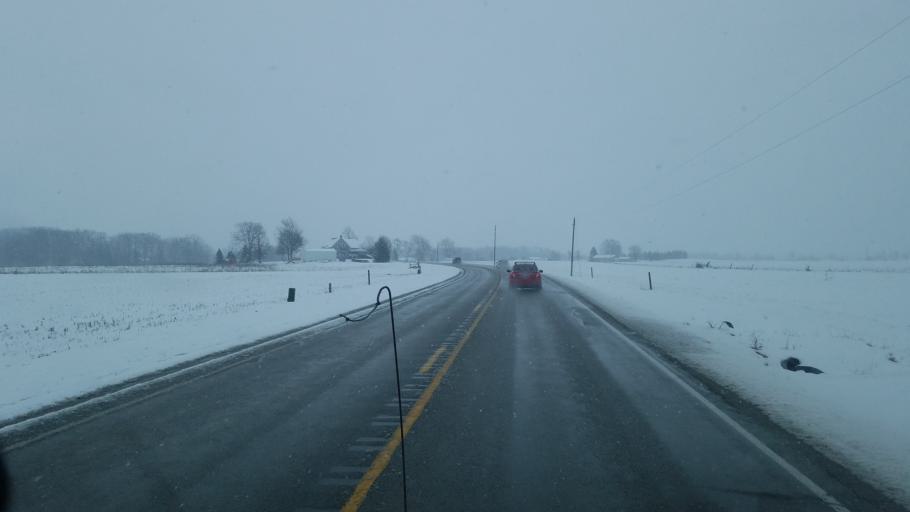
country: US
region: Indiana
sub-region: Randolph County
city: Parker City
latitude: 40.0663
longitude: -85.2630
